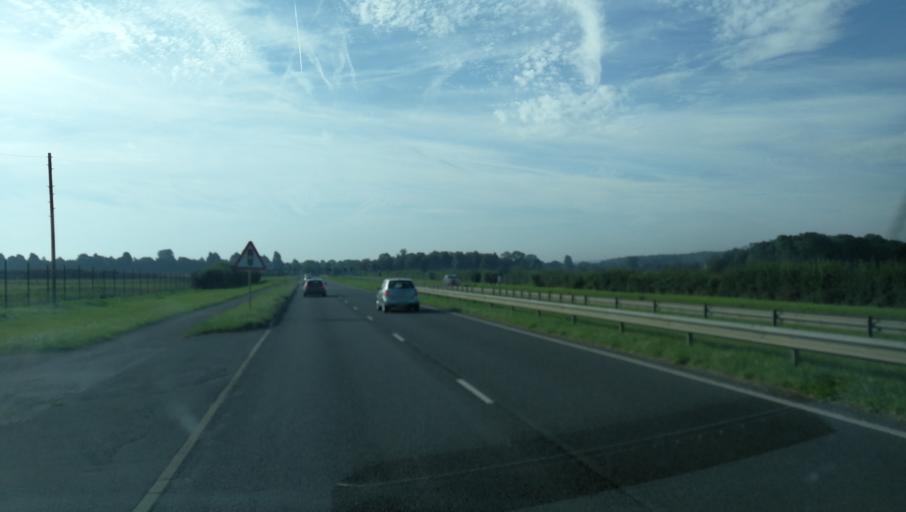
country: GB
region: England
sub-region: Oxfordshire
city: Yarnton
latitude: 51.8309
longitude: -1.3250
